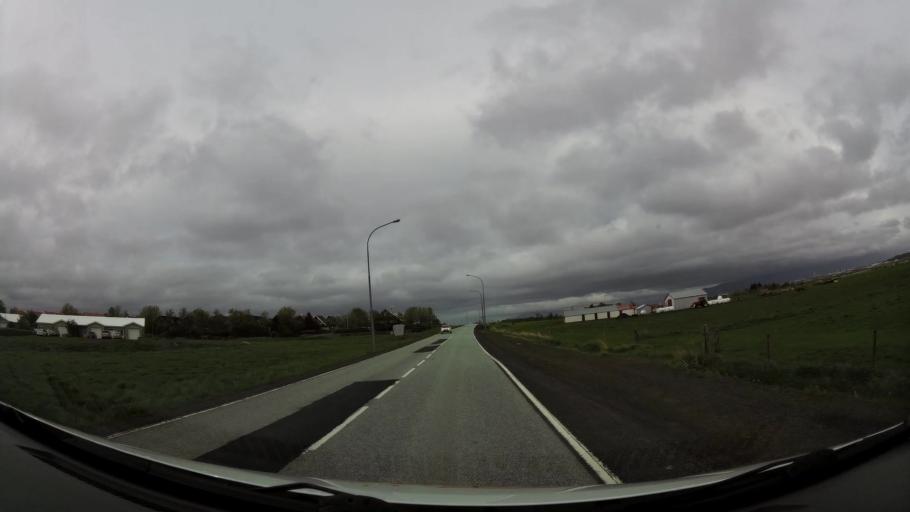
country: IS
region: Capital Region
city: Alftanes
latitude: 64.1053
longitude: -22.0097
